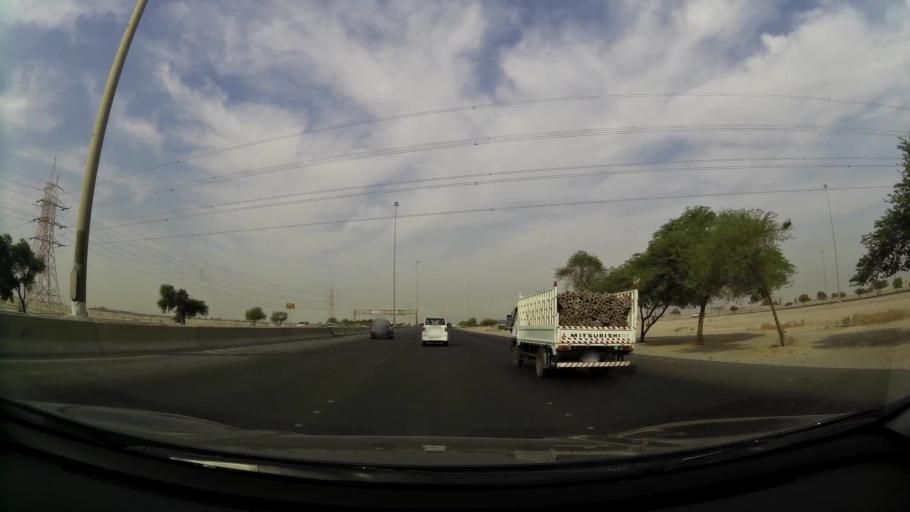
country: KW
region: Al Asimah
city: Ar Rabiyah
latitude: 29.2661
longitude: 47.8355
